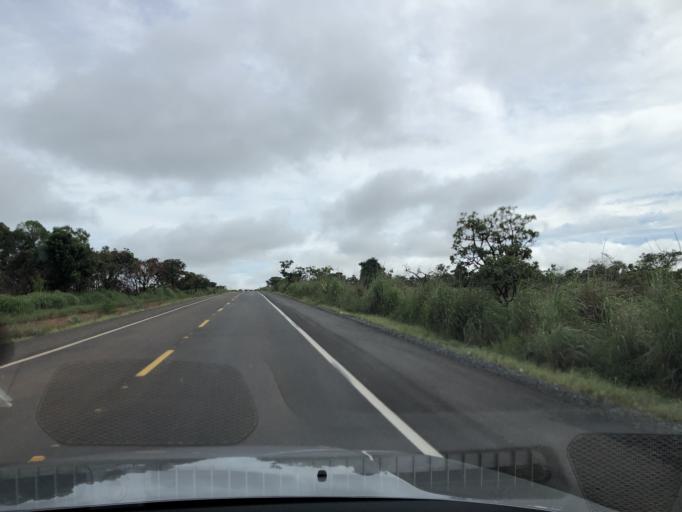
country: BR
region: Federal District
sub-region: Brasilia
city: Brasilia
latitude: -15.6378
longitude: -48.0782
